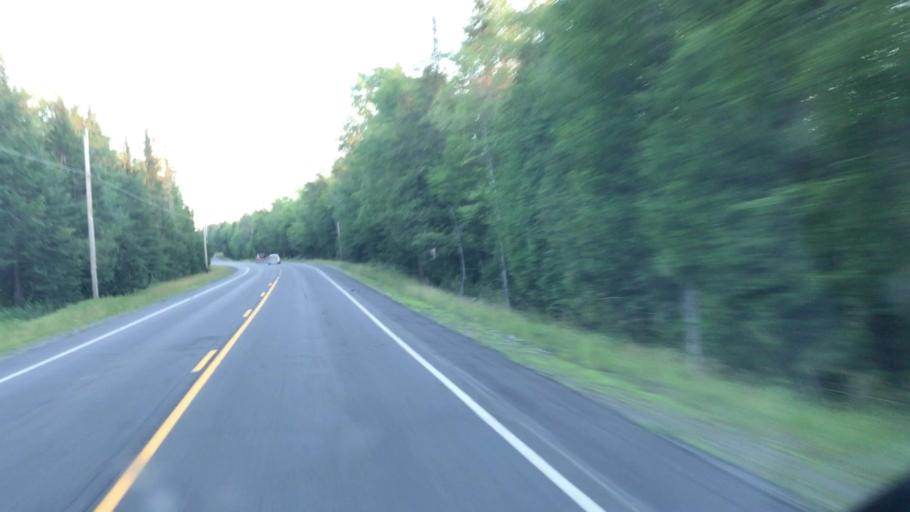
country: US
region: Maine
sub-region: Penobscot County
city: Medway
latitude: 45.5782
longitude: -68.3189
